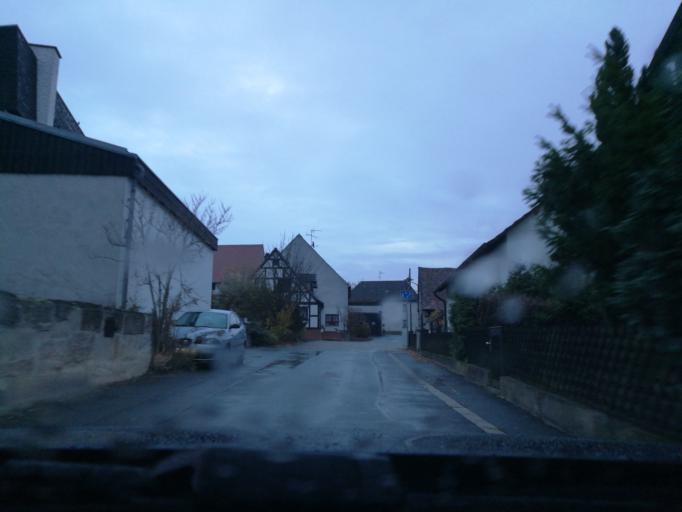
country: DE
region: Bavaria
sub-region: Regierungsbezirk Mittelfranken
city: Herzogenaurach
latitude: 49.5613
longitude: 10.9143
